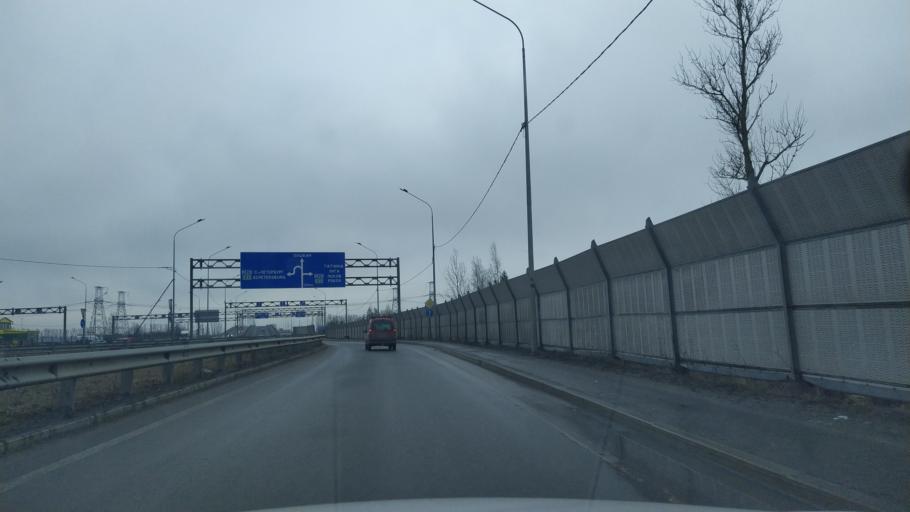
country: RU
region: St.-Petersburg
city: Aleksandrovskaya
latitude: 59.7205
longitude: 30.2717
